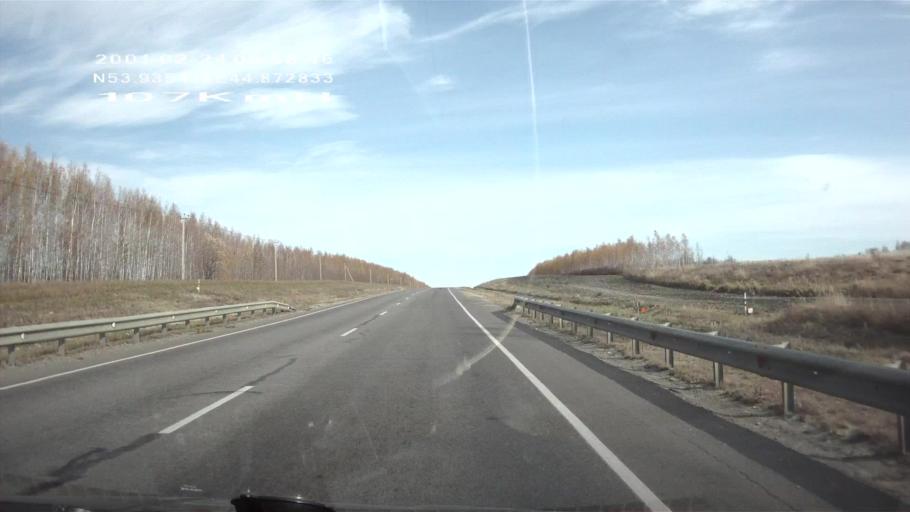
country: RU
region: Penza
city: Issa
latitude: 53.9360
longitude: 44.8733
